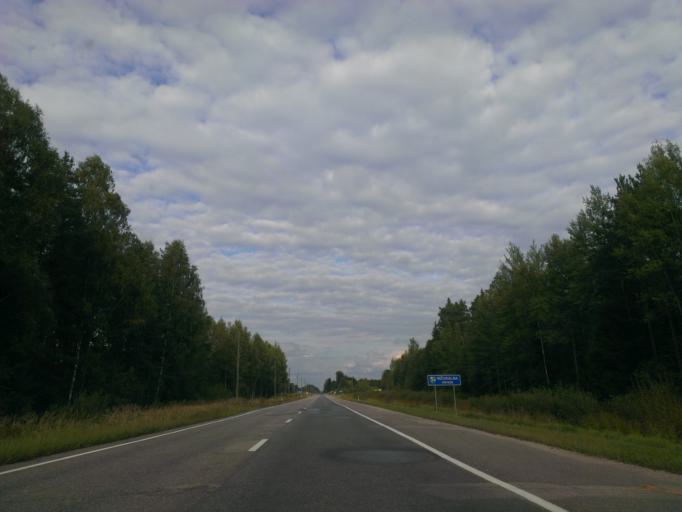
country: LV
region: Incukalns
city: Vangazi
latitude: 57.0856
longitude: 24.5411
